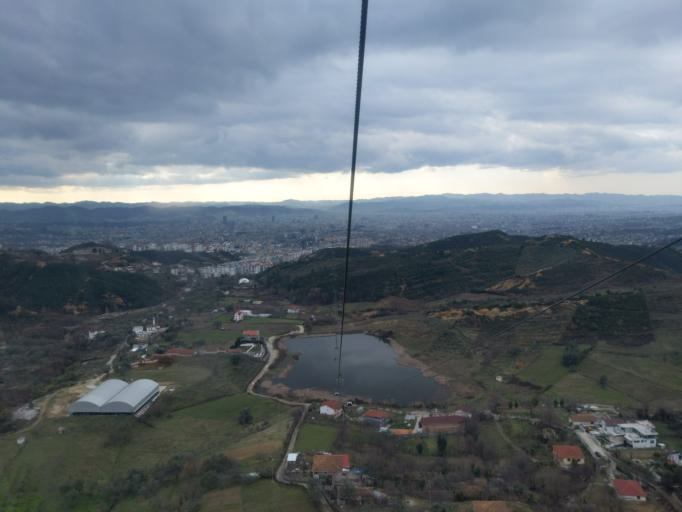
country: AL
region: Tirane
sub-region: Rrethi i Tiranes
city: Dajt
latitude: 41.3590
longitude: 19.8817
